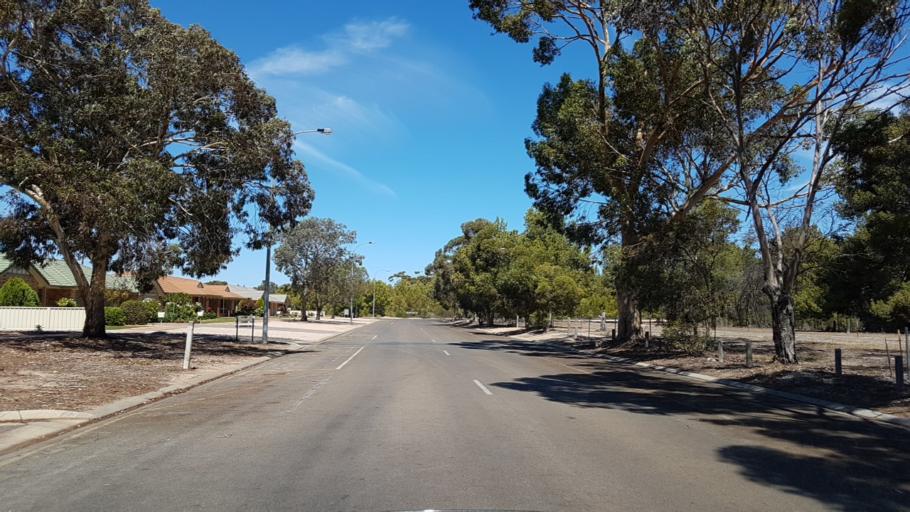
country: AU
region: South Australia
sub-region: Copper Coast
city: Wallaroo
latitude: -34.0621
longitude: 137.5900
